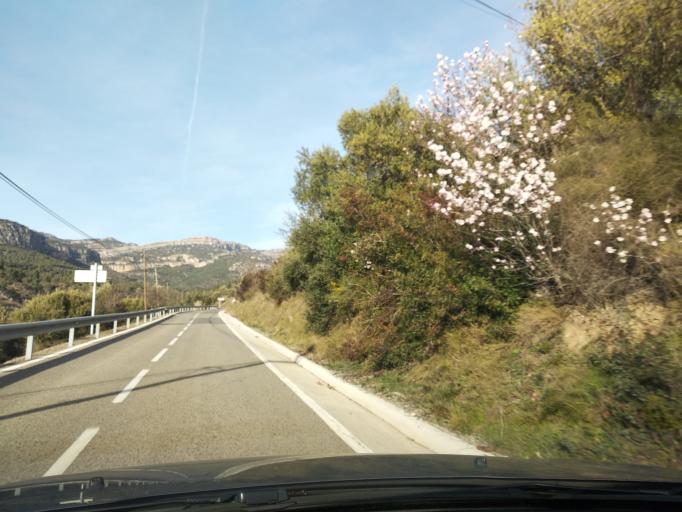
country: ES
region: Catalonia
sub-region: Provincia de Tarragona
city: Margalef
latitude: 41.2253
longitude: 0.7776
